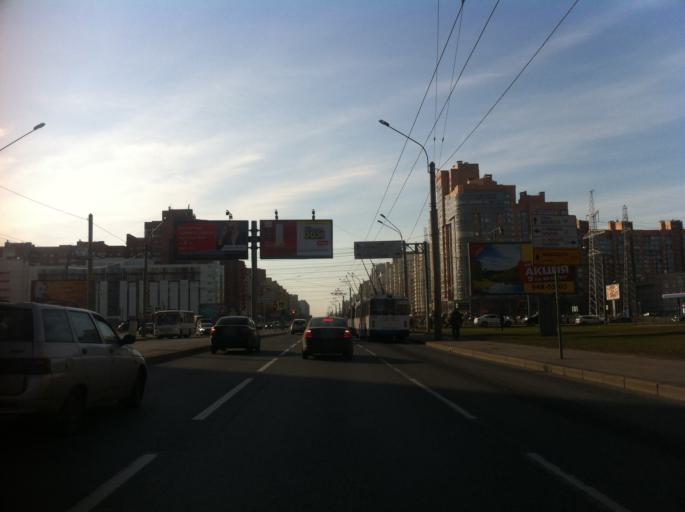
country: RU
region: St.-Petersburg
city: Uritsk
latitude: 59.8558
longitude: 30.2044
